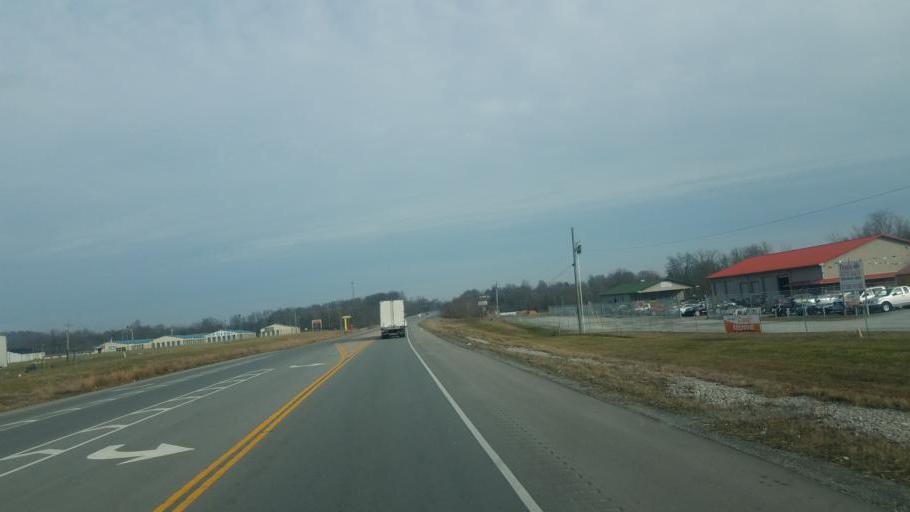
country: US
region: Kentucky
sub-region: Boyle County
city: Junction City
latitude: 37.5628
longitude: -84.7980
